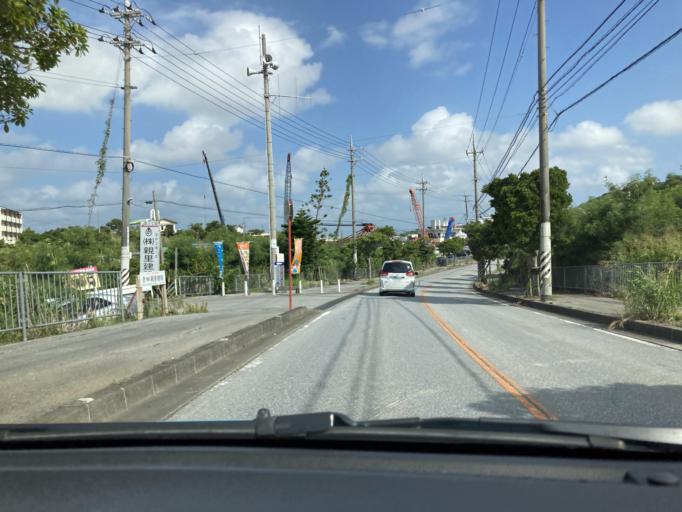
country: JP
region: Okinawa
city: Ginowan
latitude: 26.2592
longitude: 127.7764
